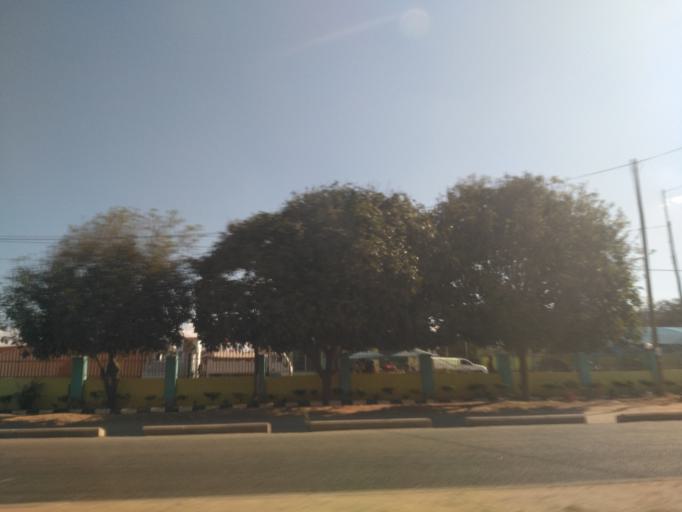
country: TZ
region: Dodoma
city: Dodoma
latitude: -6.1751
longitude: 35.7379
